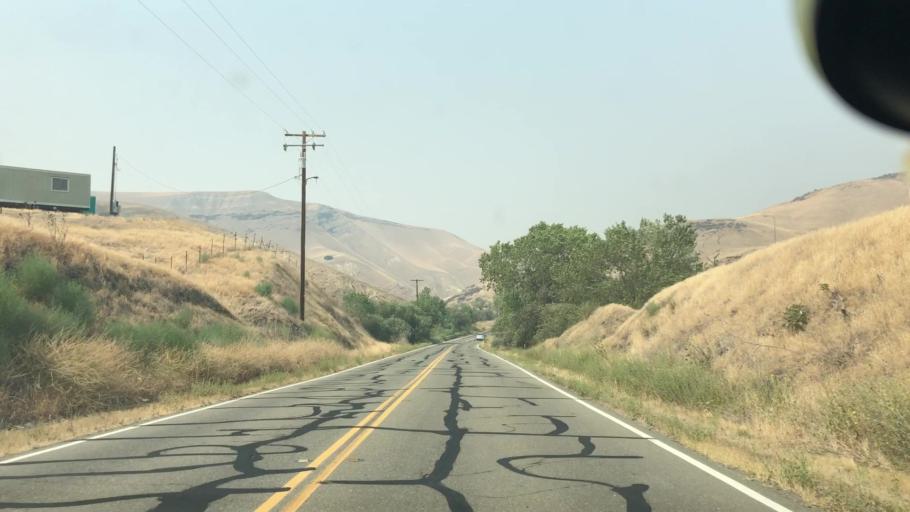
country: US
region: California
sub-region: San Joaquin County
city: Tracy
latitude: 37.6497
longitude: -121.4897
